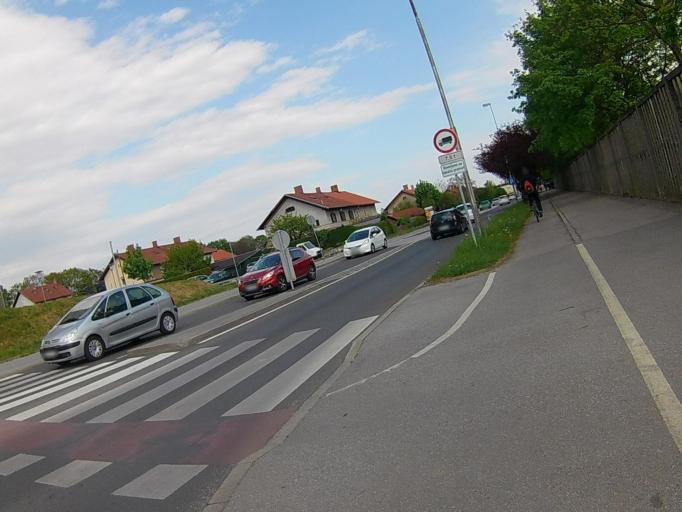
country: SI
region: Maribor
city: Maribor
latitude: 46.5509
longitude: 15.6318
